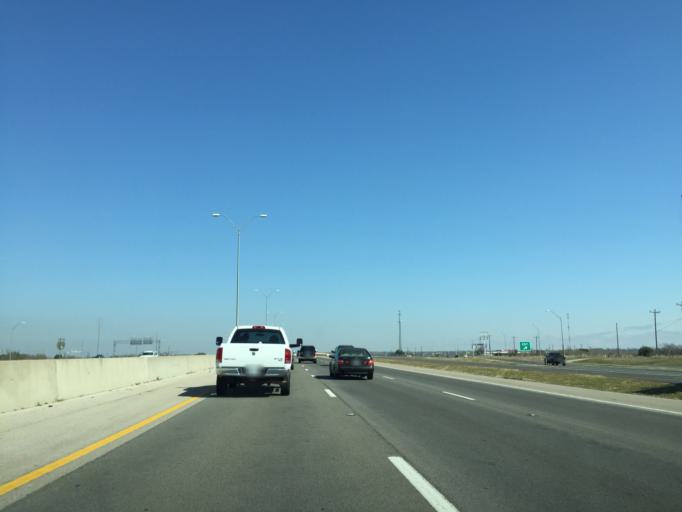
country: US
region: Texas
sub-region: Williamson County
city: Serenada
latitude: 30.6953
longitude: -97.6544
